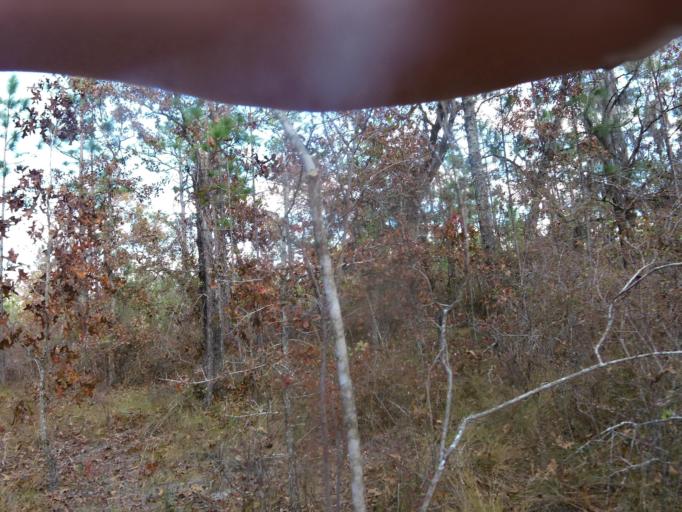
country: US
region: Florida
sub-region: Clay County
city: Middleburg
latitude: 30.1498
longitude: -81.9610
